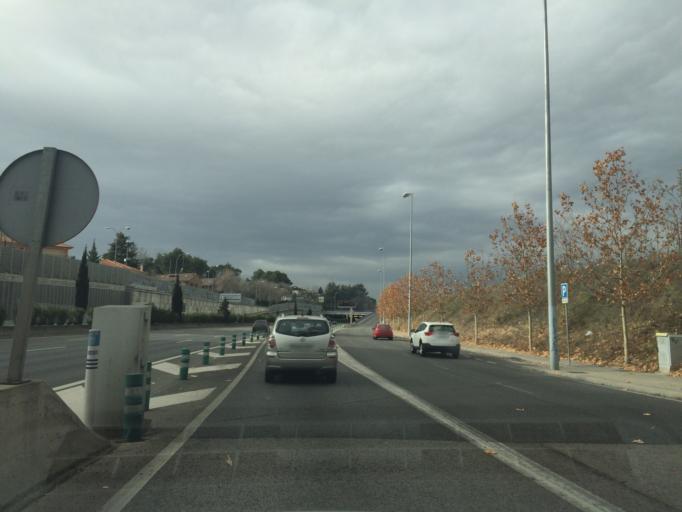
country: ES
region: Madrid
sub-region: Provincia de Madrid
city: Tetuan de las Victorias
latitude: 40.4729
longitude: -3.7307
